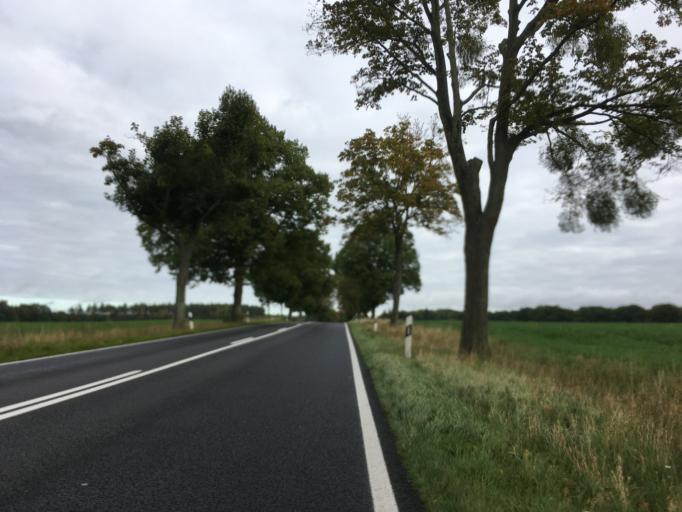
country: DE
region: Brandenburg
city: Werftpfuhl
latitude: 52.6957
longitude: 13.8667
